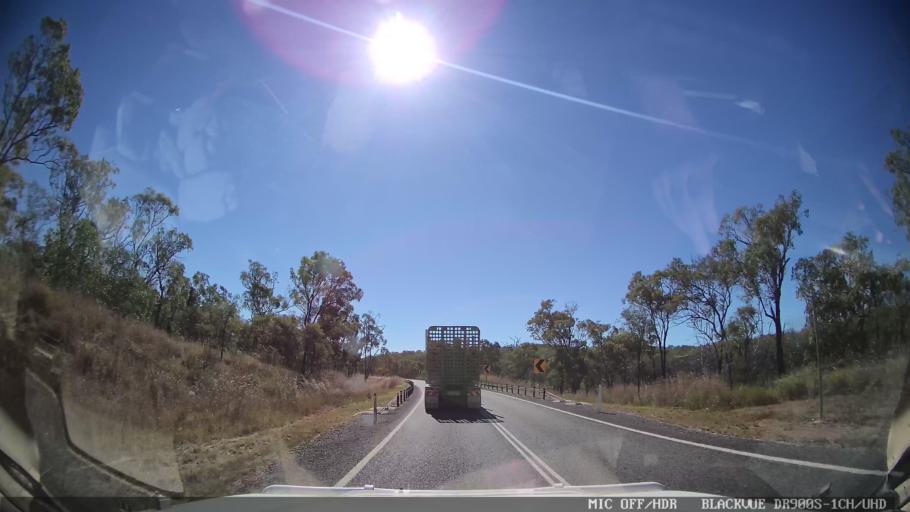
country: AU
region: Queensland
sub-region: Gladstone
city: Toolooa
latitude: -24.1528
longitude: 151.2104
